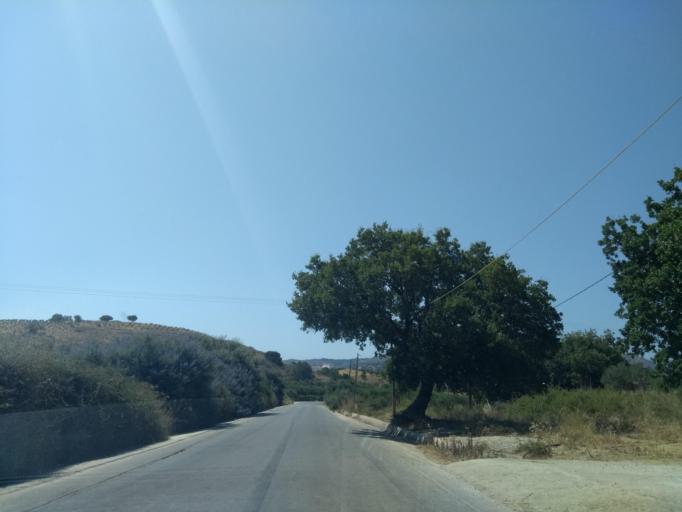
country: GR
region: Crete
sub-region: Nomos Chanias
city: Georgioupolis
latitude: 35.3546
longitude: 24.2696
